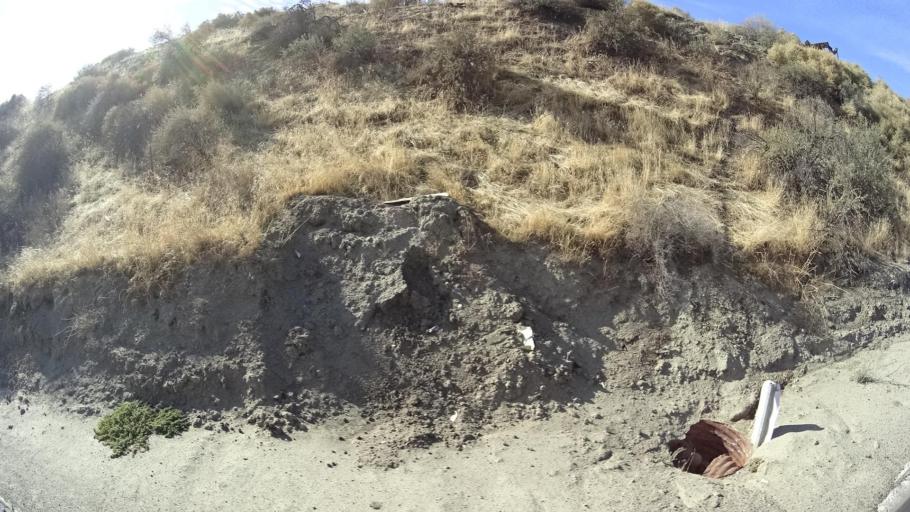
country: US
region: California
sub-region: Kern County
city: Oildale
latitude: 35.5752
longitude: -118.9603
